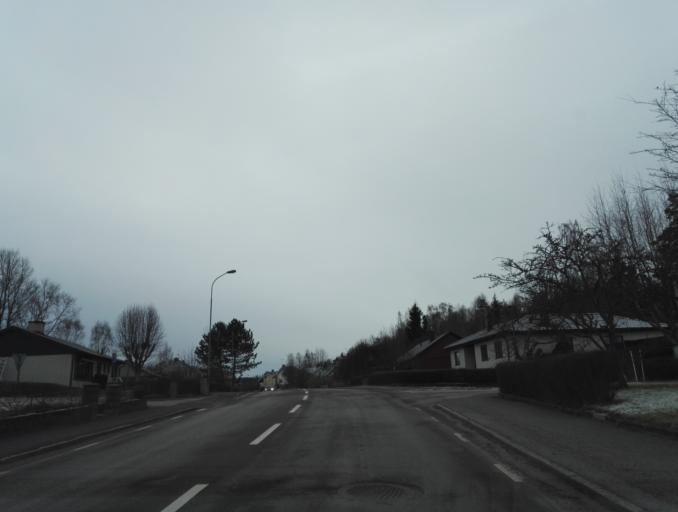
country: SE
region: Kalmar
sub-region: Hultsfreds Kommun
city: Virserum
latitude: 57.3125
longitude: 15.5847
